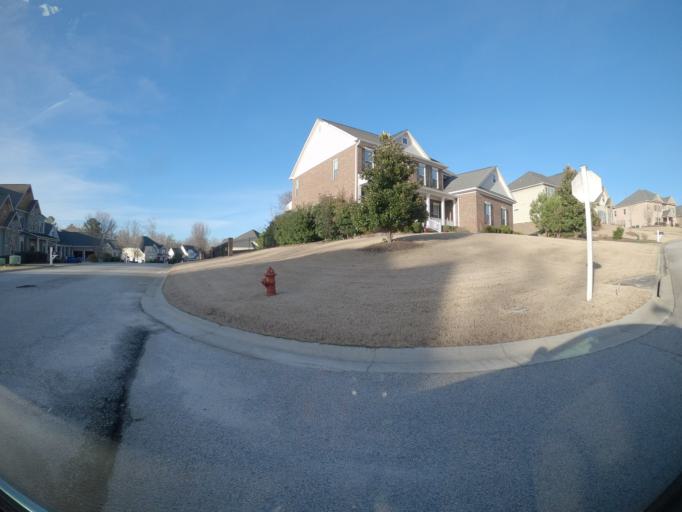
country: US
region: Georgia
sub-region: Columbia County
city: Evans
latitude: 33.5902
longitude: -82.2015
